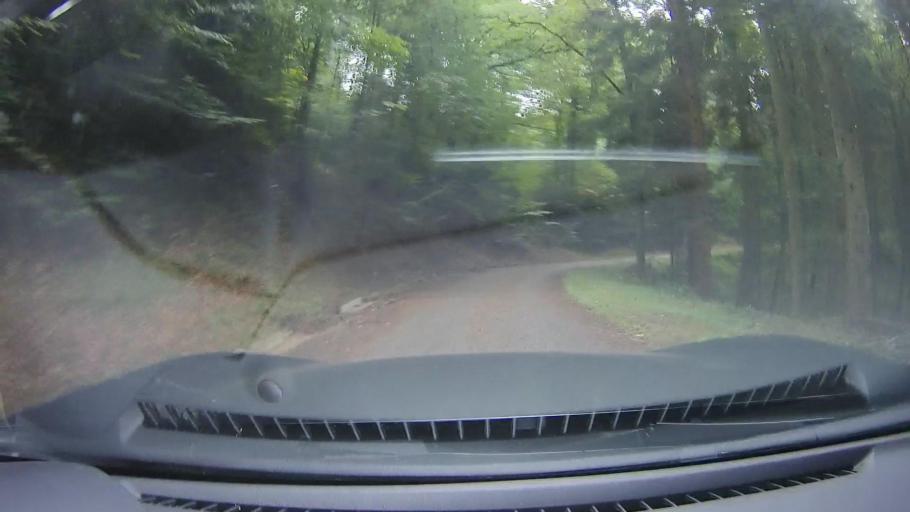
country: DE
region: Baden-Wuerttemberg
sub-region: Regierungsbezirk Stuttgart
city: Kaisersbach
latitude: 48.9548
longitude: 9.6455
